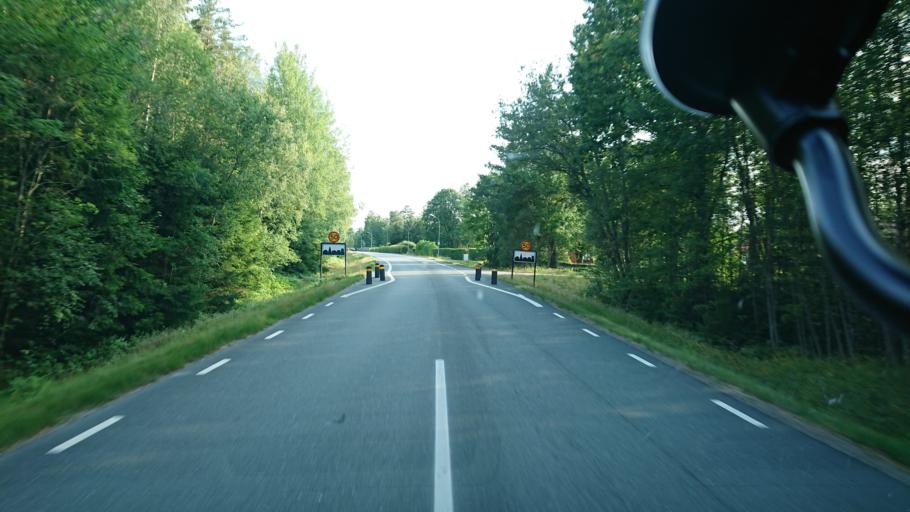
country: SE
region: Kronoberg
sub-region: Vaxjo Kommun
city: Rottne
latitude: 57.0327
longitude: 14.8978
